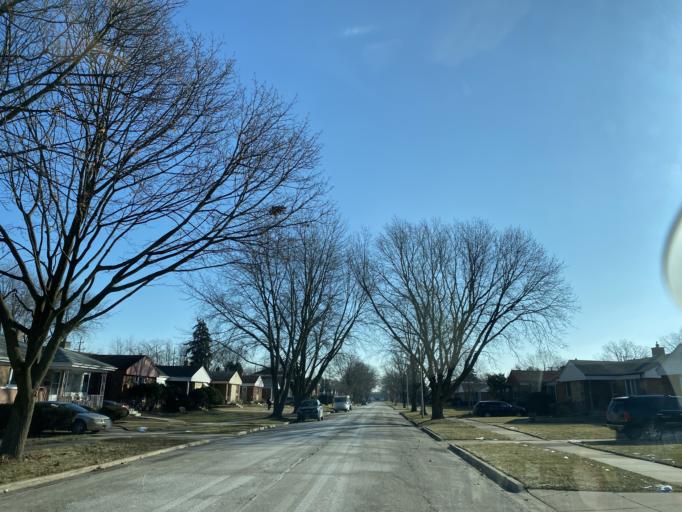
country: US
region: Illinois
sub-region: Cook County
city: Westchester
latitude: 41.8617
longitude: -87.8722
